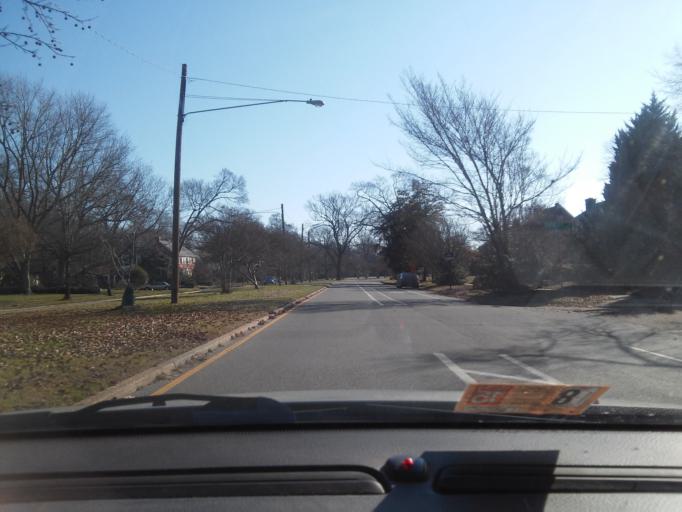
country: US
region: Virginia
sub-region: City of Richmond
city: Richmond
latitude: 37.5757
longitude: -77.4575
